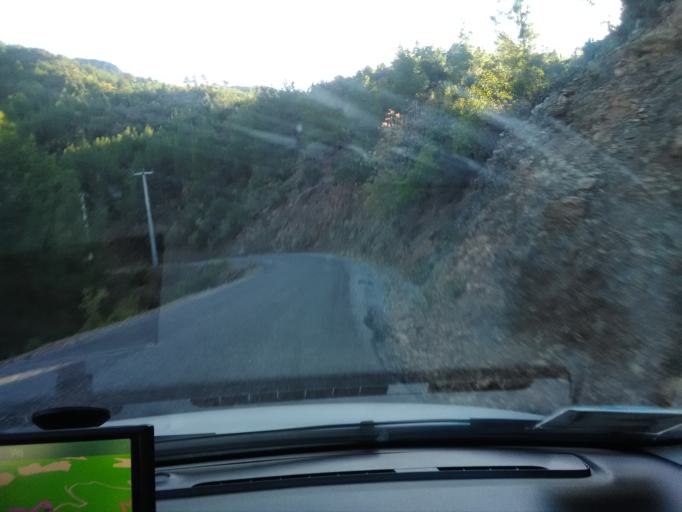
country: TR
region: Antalya
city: Gazipasa
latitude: 36.3052
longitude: 32.3999
